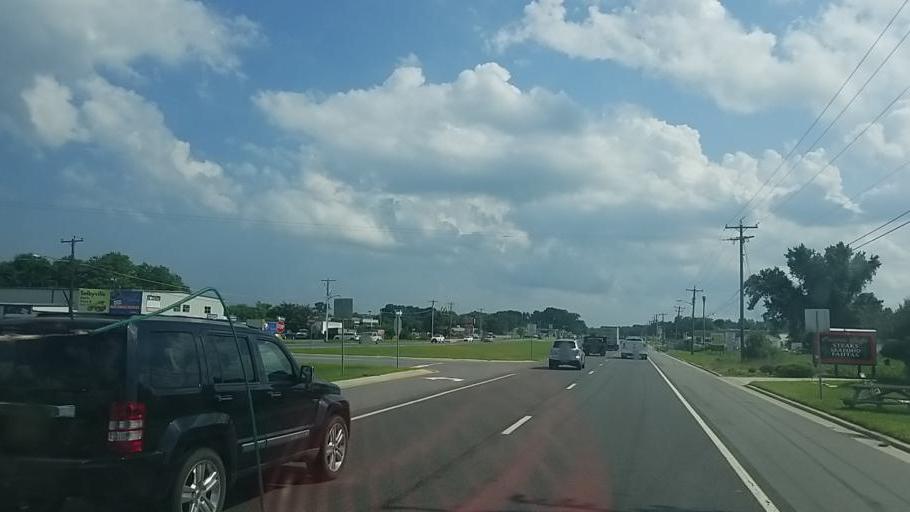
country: US
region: Delaware
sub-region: Sussex County
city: Selbyville
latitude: 38.4612
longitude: -75.2340
